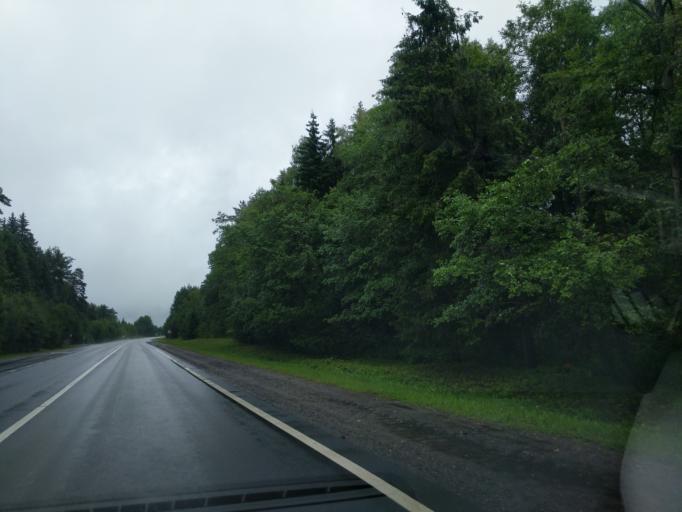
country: BY
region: Minsk
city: Syomkava
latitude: 54.1725
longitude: 27.4995
